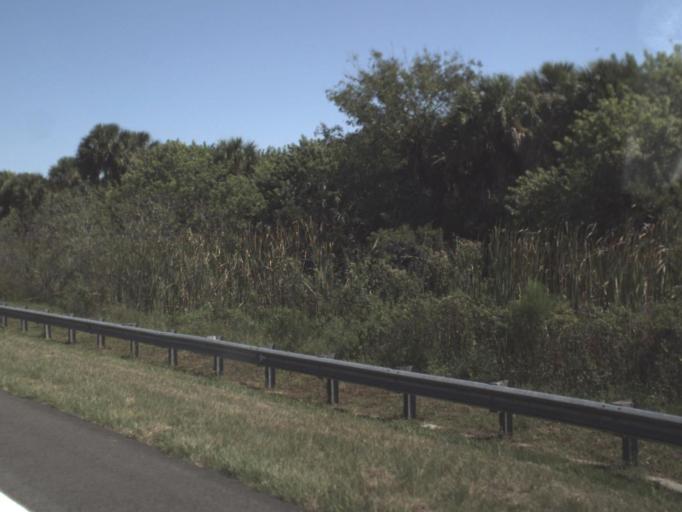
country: US
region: Florida
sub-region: Glades County
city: Buckhead Ridge
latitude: 27.0303
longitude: -81.0073
